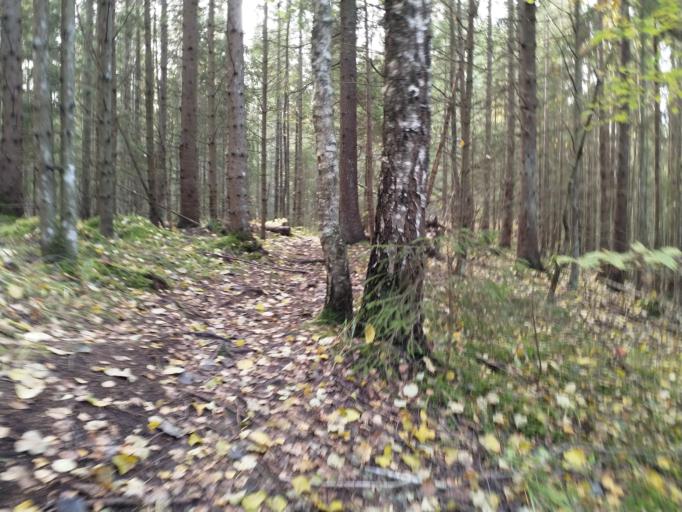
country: LV
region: Dundaga
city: Dundaga
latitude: 57.6470
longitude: 22.2624
